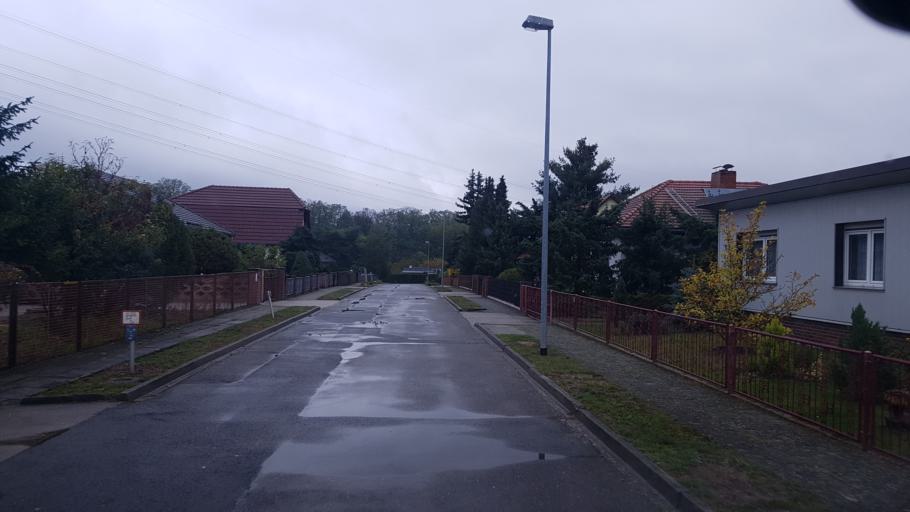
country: DE
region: Brandenburg
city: Altdobern
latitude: 51.6503
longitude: 14.0140
